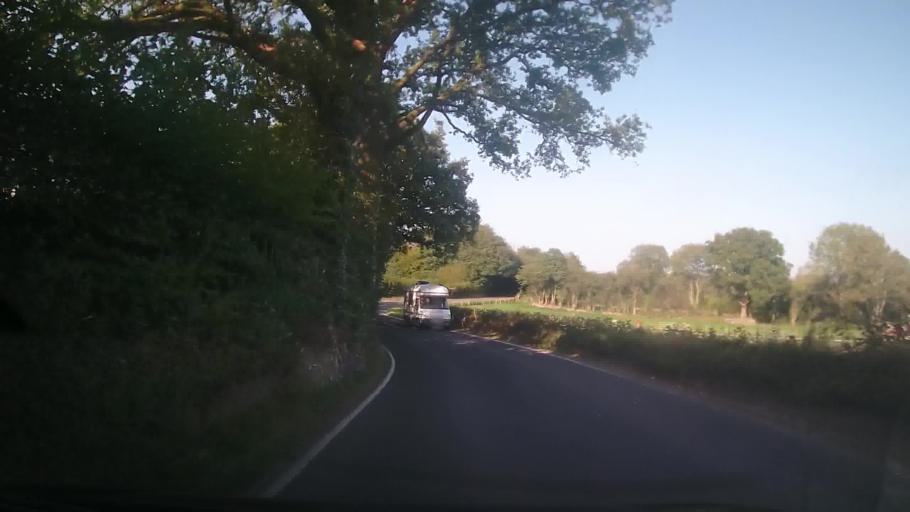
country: GB
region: Wales
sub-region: County of Ceredigion
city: Llangybi
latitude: 52.1822
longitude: -4.0012
